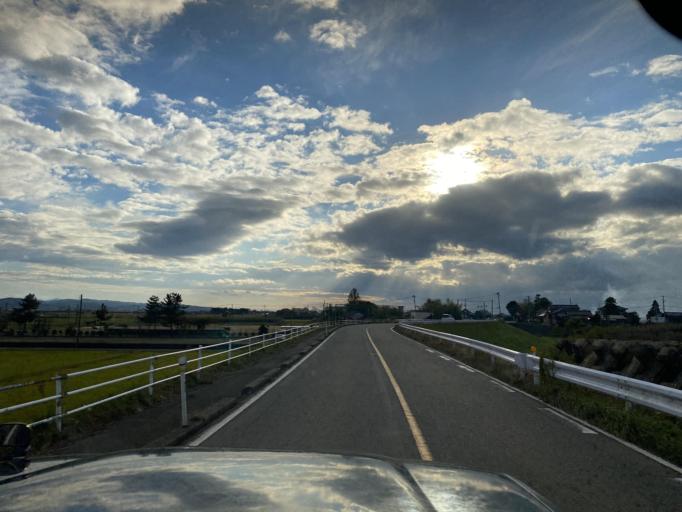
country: JP
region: Niigata
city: Kamo
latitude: 37.6832
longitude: 139.0221
